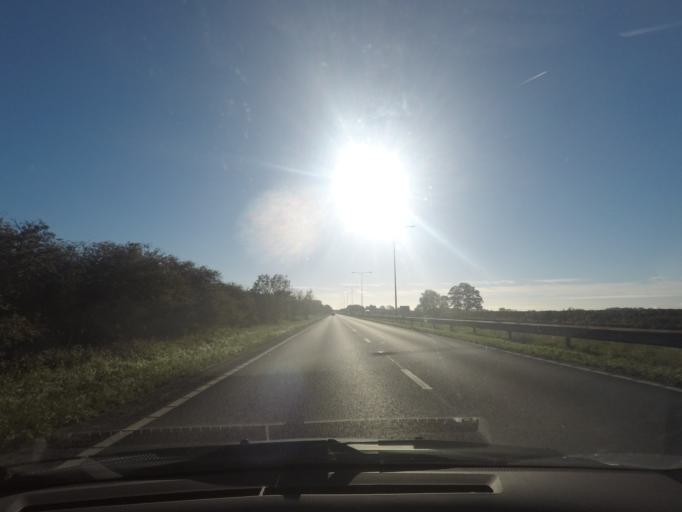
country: GB
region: England
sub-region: East Riding of Yorkshire
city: Brantingham
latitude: 53.7548
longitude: -0.5839
